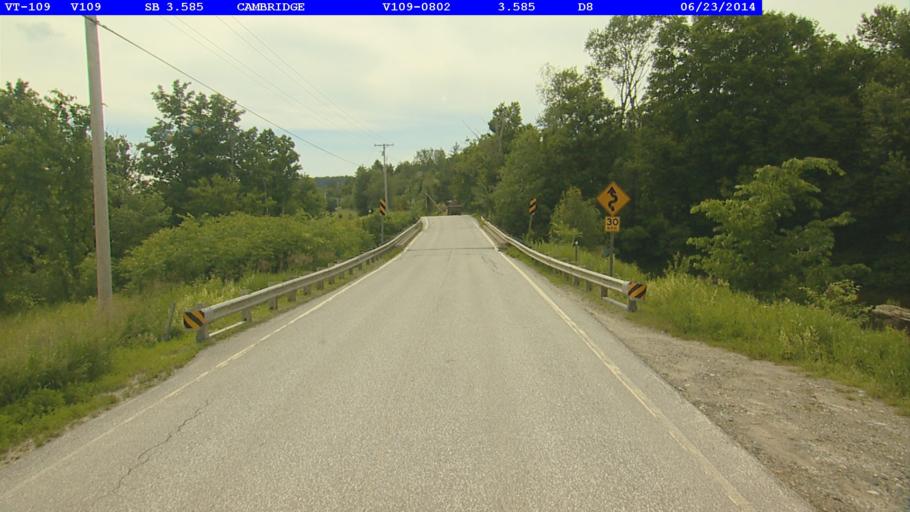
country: US
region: Vermont
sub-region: Lamoille County
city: Johnson
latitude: 44.6824
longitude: -72.7762
